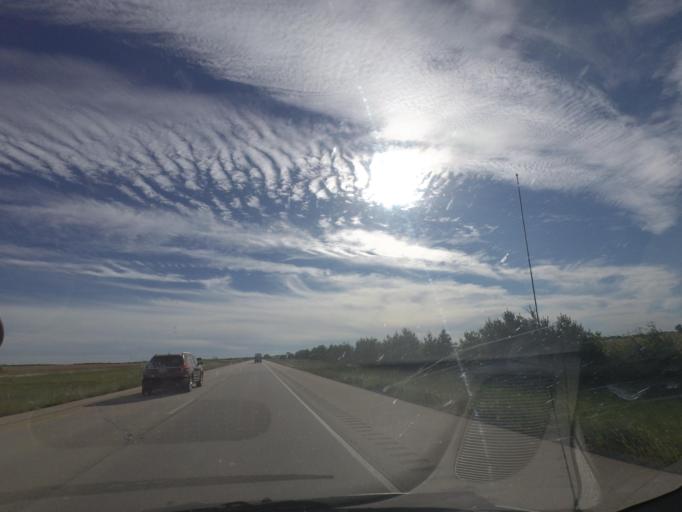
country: US
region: Illinois
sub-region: Piatt County
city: Cerro Gordo
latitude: 39.9443
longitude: -88.8320
